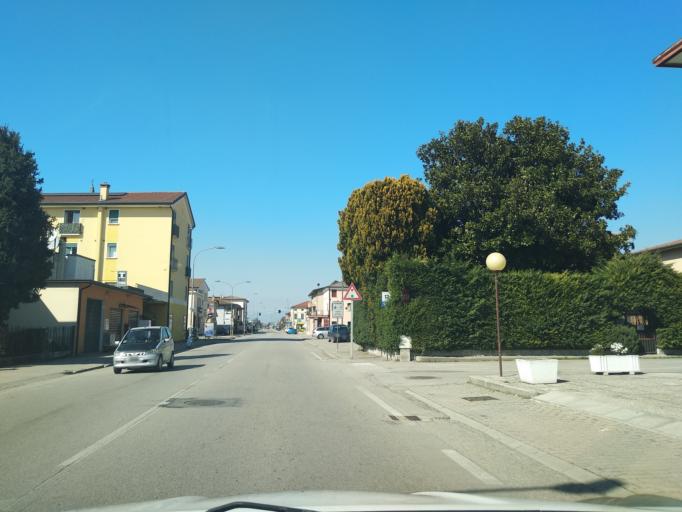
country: IT
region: Veneto
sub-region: Provincia di Padova
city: Villafranca Padovana
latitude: 45.4935
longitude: 11.7991
